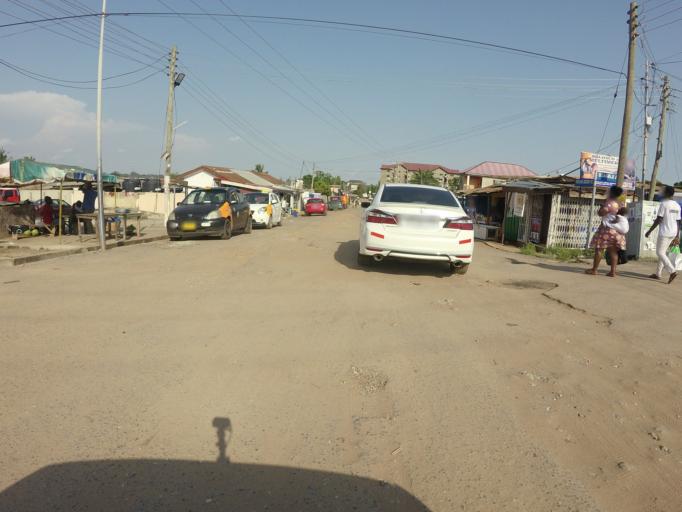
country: GH
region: Greater Accra
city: Dome
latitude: 5.6130
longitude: -0.2399
